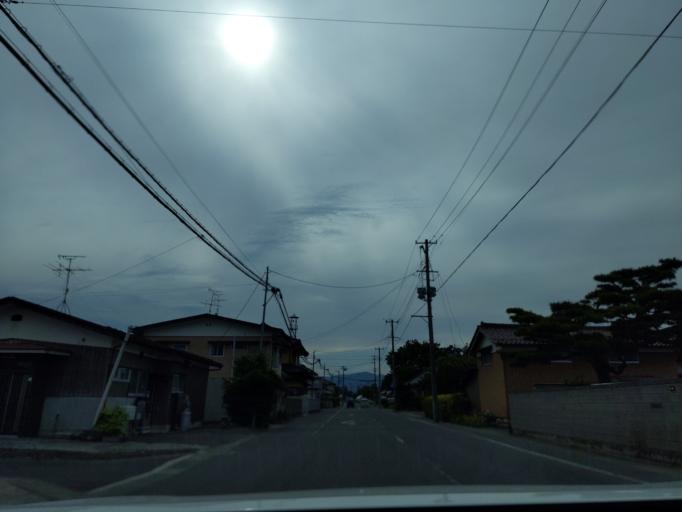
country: JP
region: Fukushima
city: Koriyama
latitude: 37.3749
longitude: 140.3252
